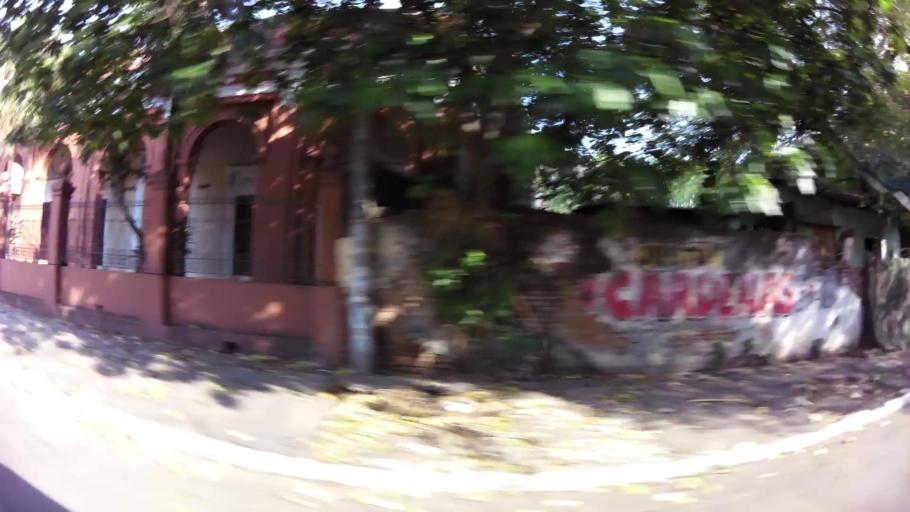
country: PY
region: Asuncion
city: Asuncion
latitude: -25.2836
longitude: -57.6208
